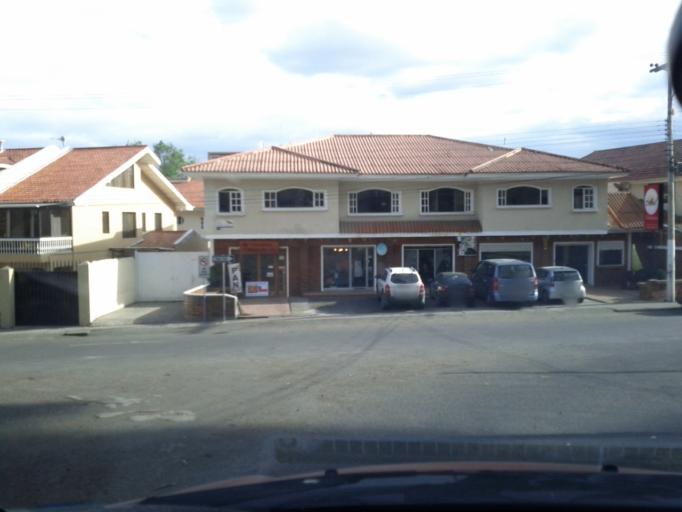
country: EC
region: Azuay
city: Cuenca
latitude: -2.8916
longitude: -79.0292
